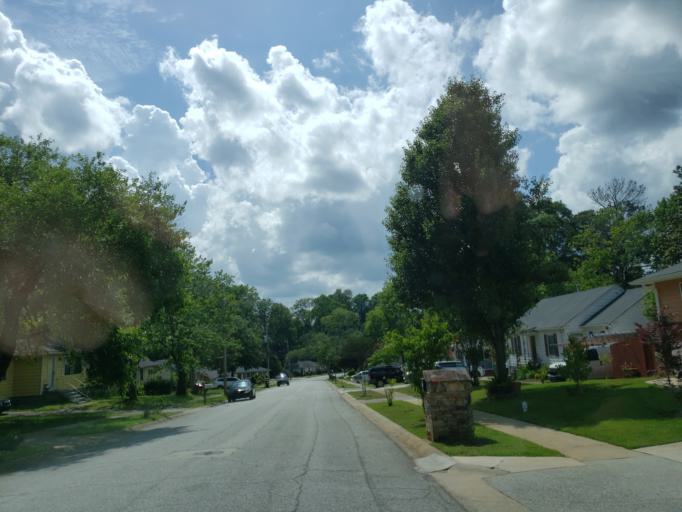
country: US
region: Georgia
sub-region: Cobb County
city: Smyrna
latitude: 33.8935
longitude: -84.5331
